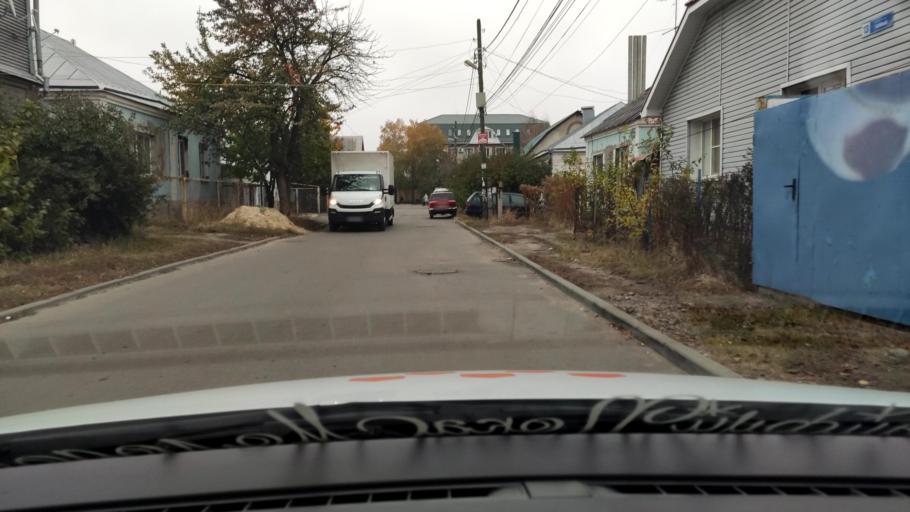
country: RU
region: Voronezj
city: Voronezh
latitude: 51.6740
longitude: 39.1348
